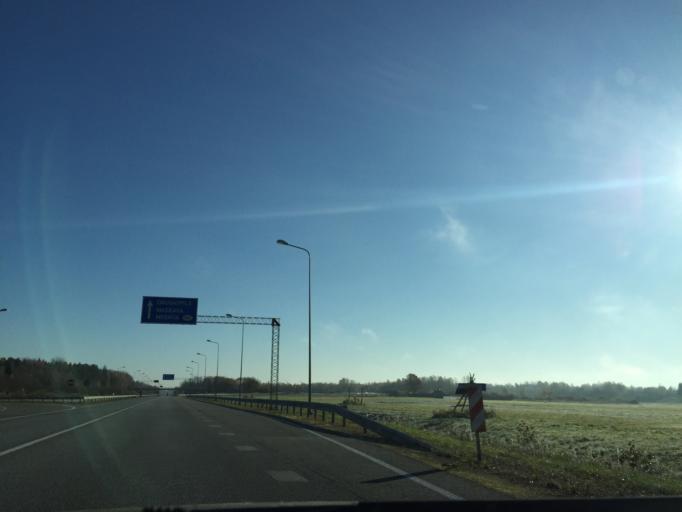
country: LV
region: Aizkraukles Rajons
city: Aizkraukle
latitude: 56.7027
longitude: 25.2726
